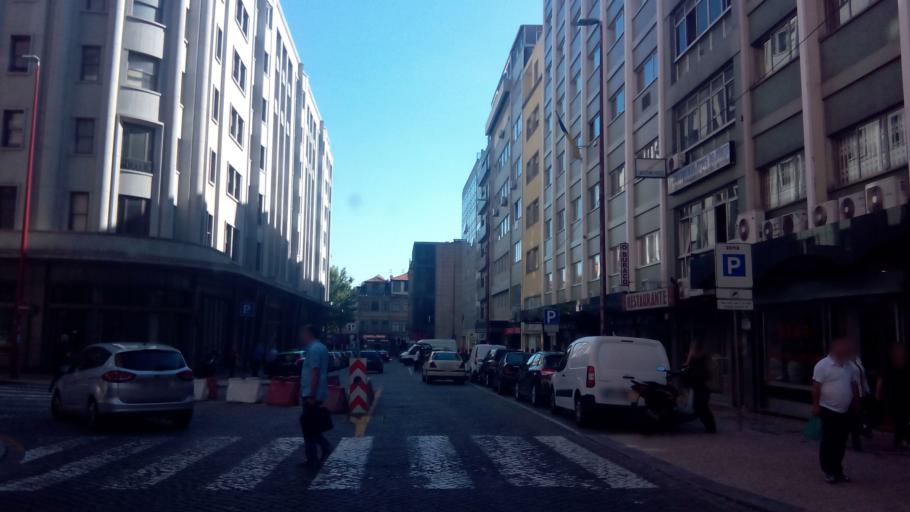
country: PT
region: Porto
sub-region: Porto
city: Porto
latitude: 41.1513
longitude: -8.6074
